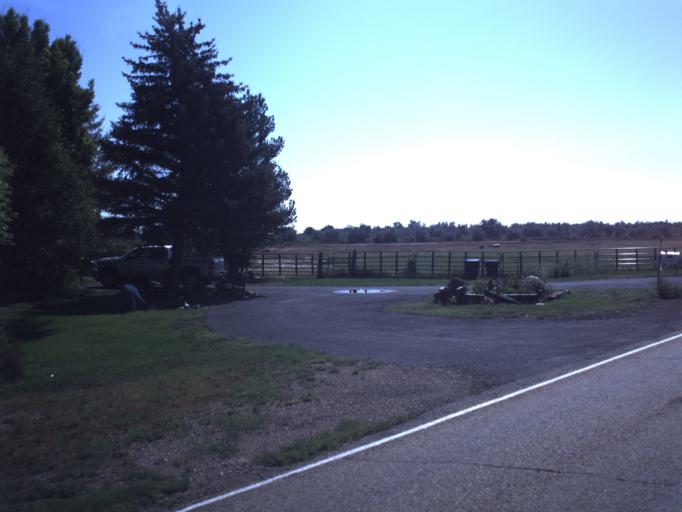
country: US
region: Utah
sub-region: Duchesne County
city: Duchesne
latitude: 40.3301
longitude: -110.2697
